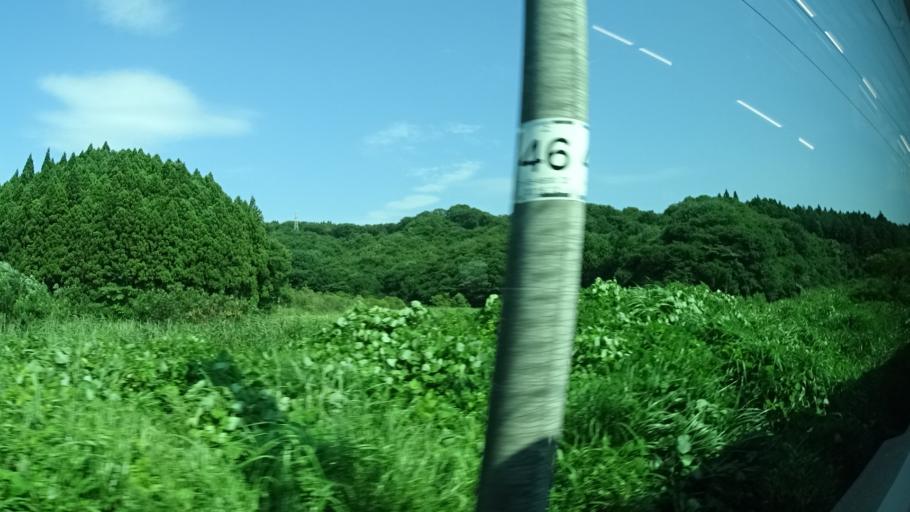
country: JP
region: Miyagi
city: Kogota
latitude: 38.4952
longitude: 141.0878
